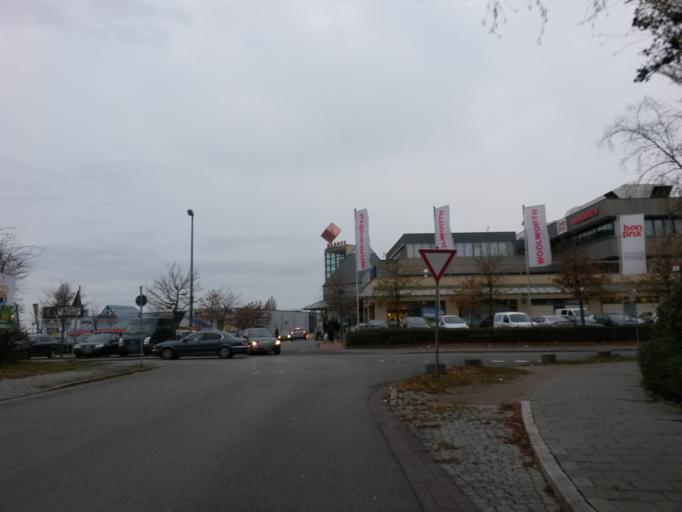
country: DE
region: Bremen
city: Bremen
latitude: 53.0478
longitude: 8.8502
